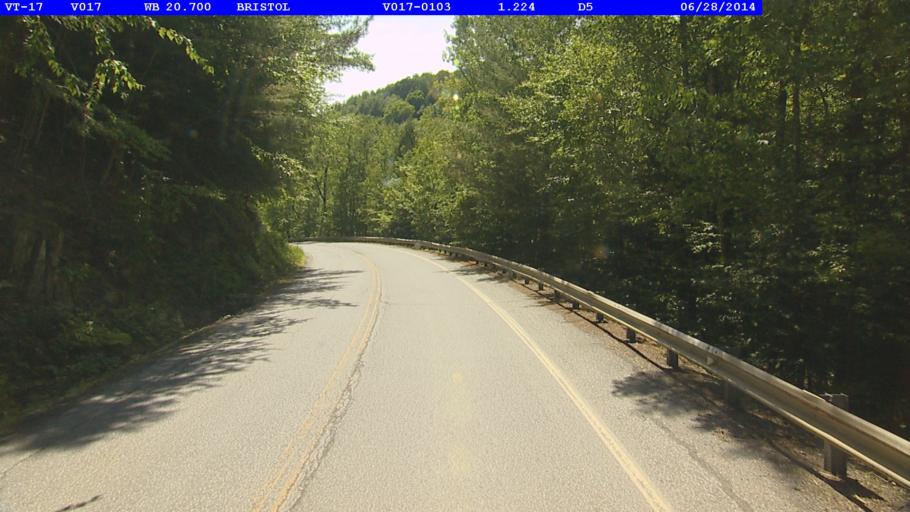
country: US
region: Vermont
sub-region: Addison County
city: Bristol
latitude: 44.1602
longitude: -73.0383
